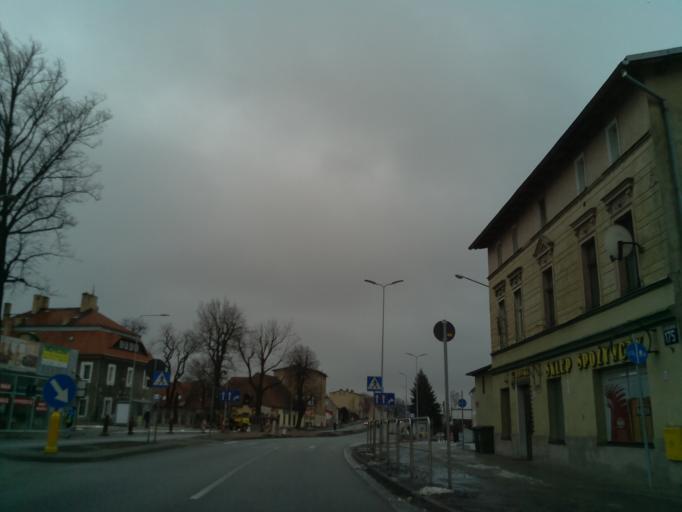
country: PL
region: Lower Silesian Voivodeship
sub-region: Powiat swidnicki
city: Swiebodzice
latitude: 50.8271
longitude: 16.3047
